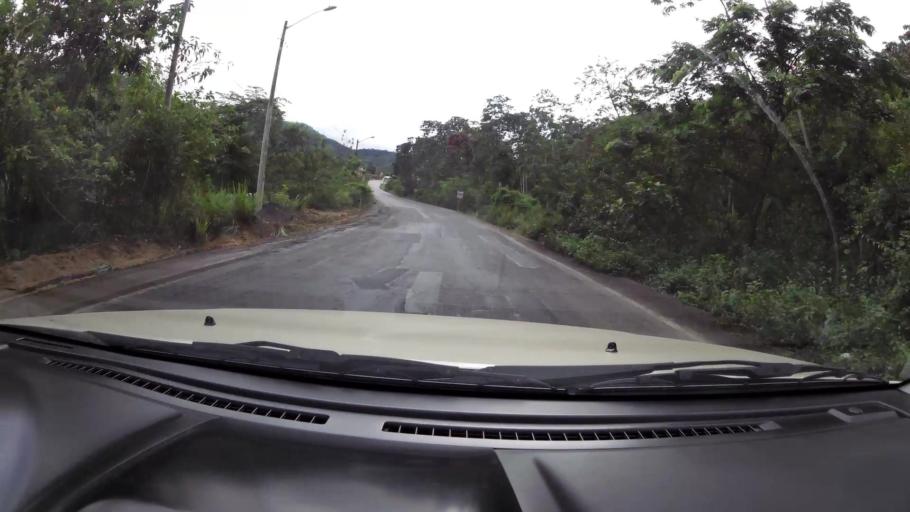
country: EC
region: El Oro
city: Pasaje
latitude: -3.3211
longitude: -79.6808
